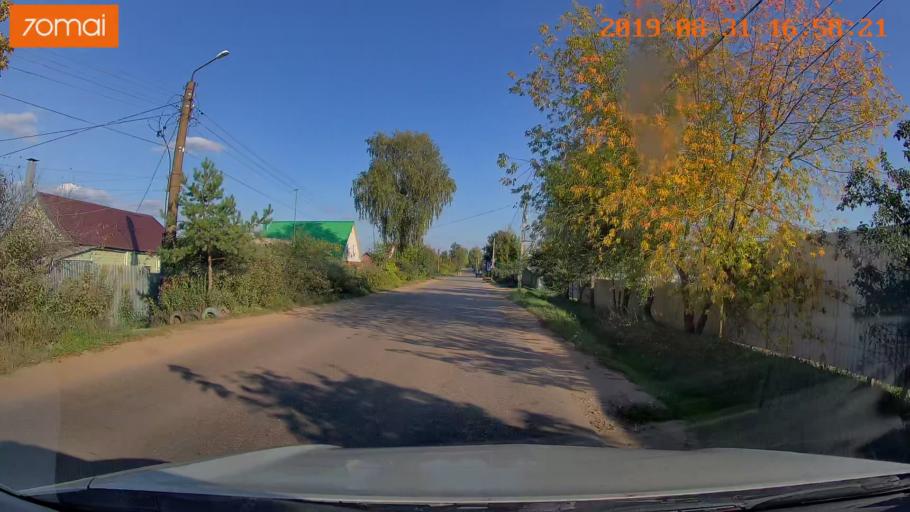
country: RU
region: Kaluga
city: Detchino
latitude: 54.8159
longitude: 36.3018
